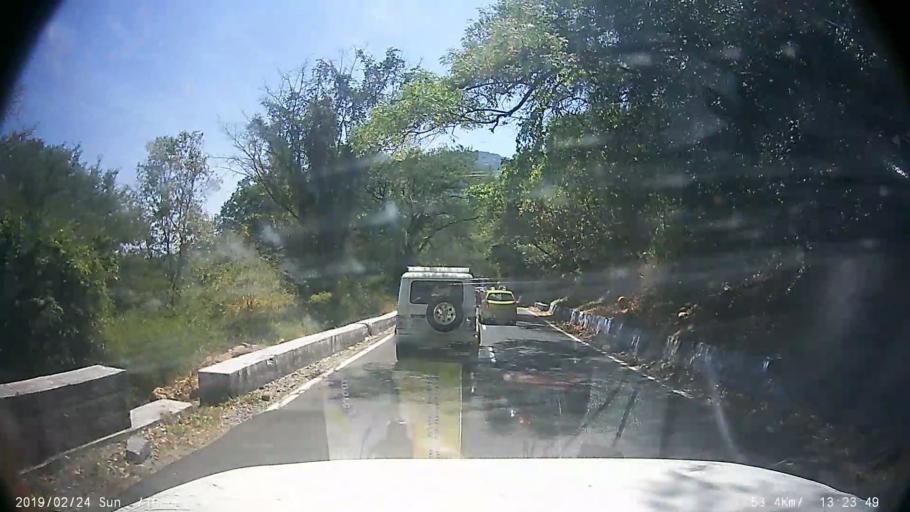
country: IN
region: Tamil Nadu
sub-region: Coimbatore
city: Mettupalayam
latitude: 11.3444
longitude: 76.8746
